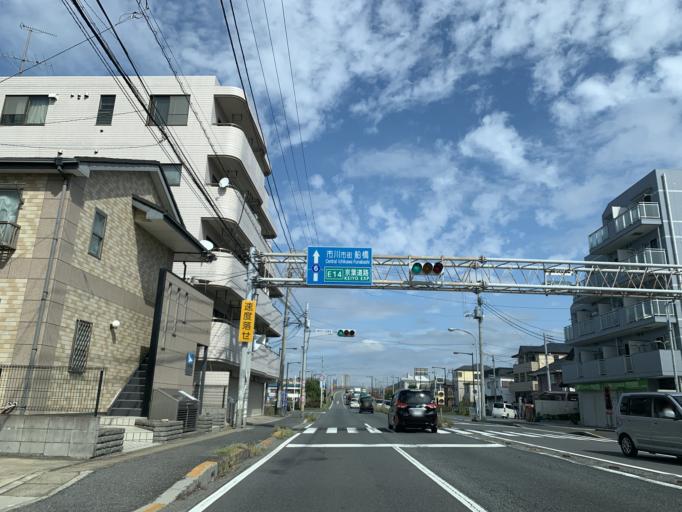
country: JP
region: Tokyo
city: Urayasu
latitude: 35.6970
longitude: 139.9236
